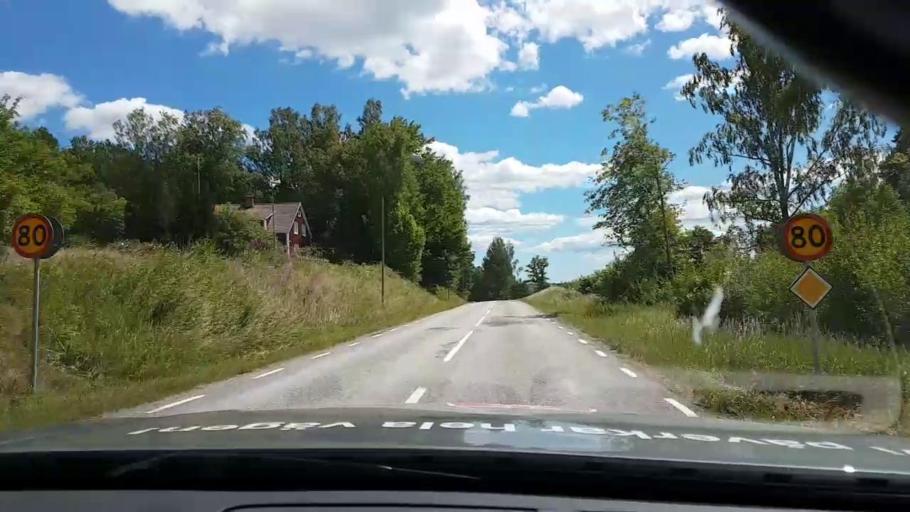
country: SE
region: Kalmar
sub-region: Vasterviks Kommun
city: Overum
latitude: 58.0787
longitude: 16.3558
